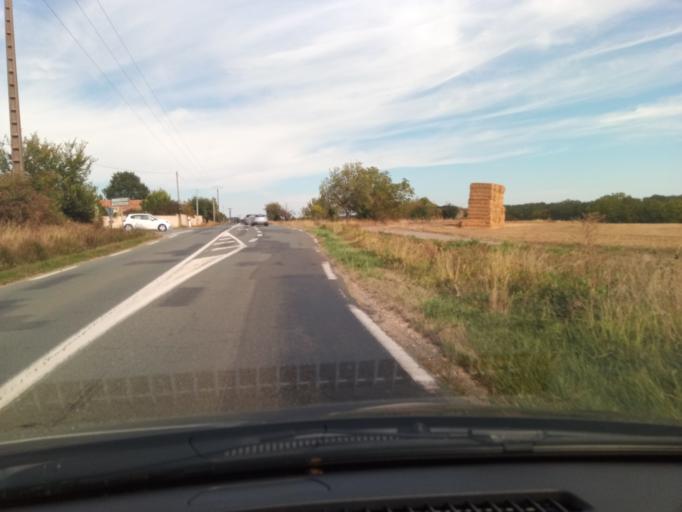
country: FR
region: Poitou-Charentes
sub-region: Departement de la Vienne
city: Chauvigny
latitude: 46.5565
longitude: 0.6129
